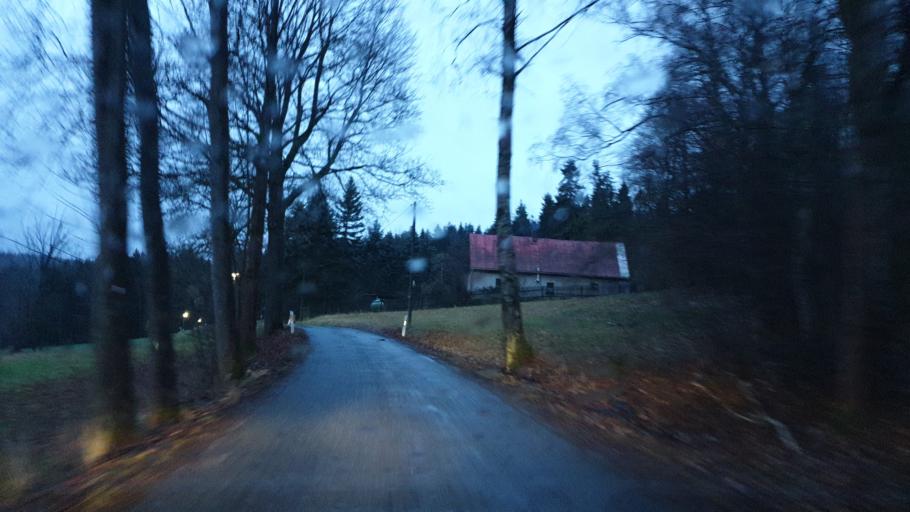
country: DE
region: Saxony
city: Bad Elster
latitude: 50.3066
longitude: 12.2358
